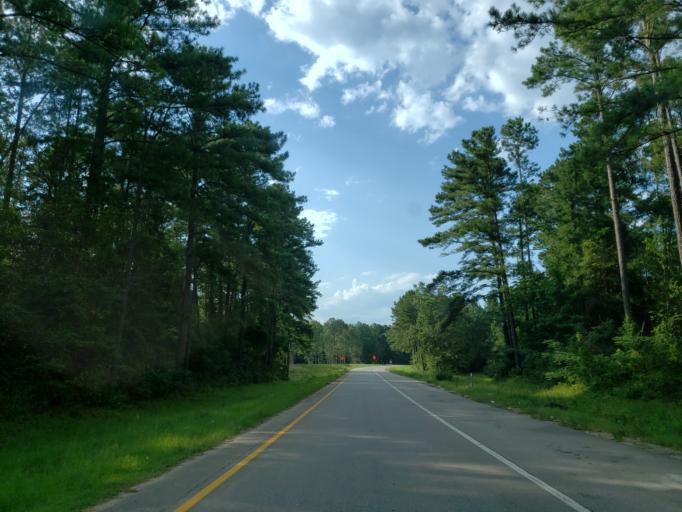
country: US
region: Mississippi
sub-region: Clarke County
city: Stonewall
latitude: 32.1645
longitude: -88.8659
